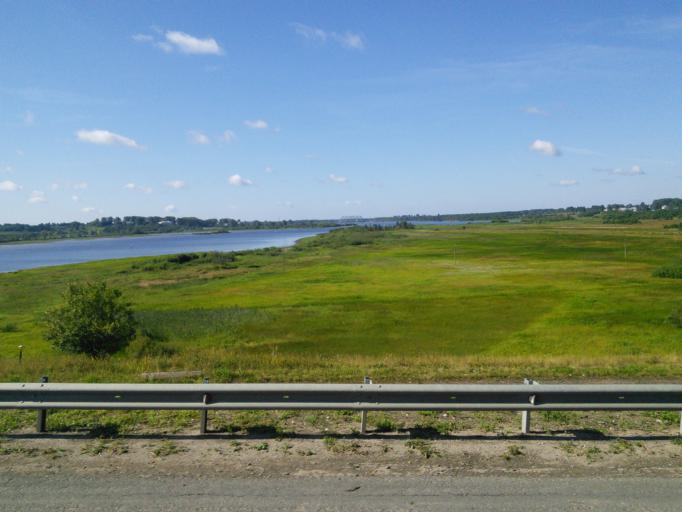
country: RU
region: Vologda
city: Sheksna
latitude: 59.2152
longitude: 38.4913
